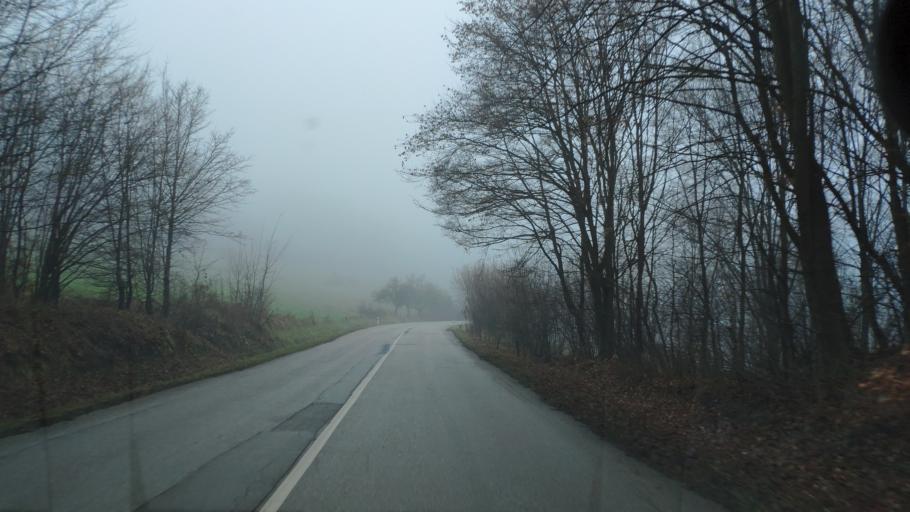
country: SK
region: Kosicky
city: Roznava
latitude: 48.6395
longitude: 20.3589
